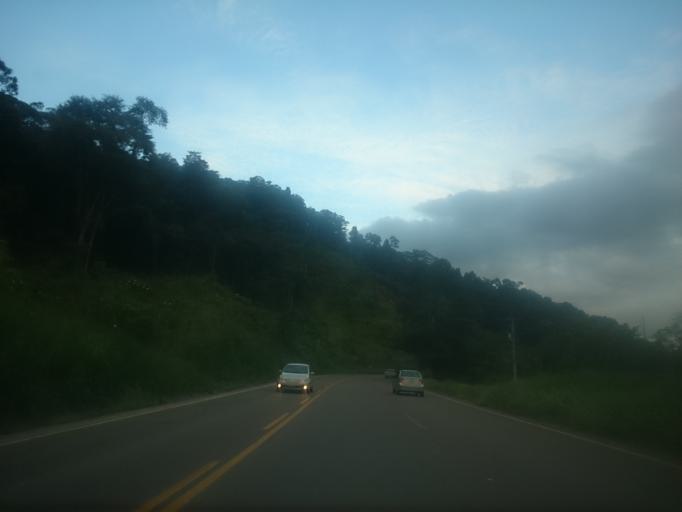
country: BR
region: Santa Catarina
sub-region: Blumenau
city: Blumenau
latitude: -26.8717
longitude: -49.0168
